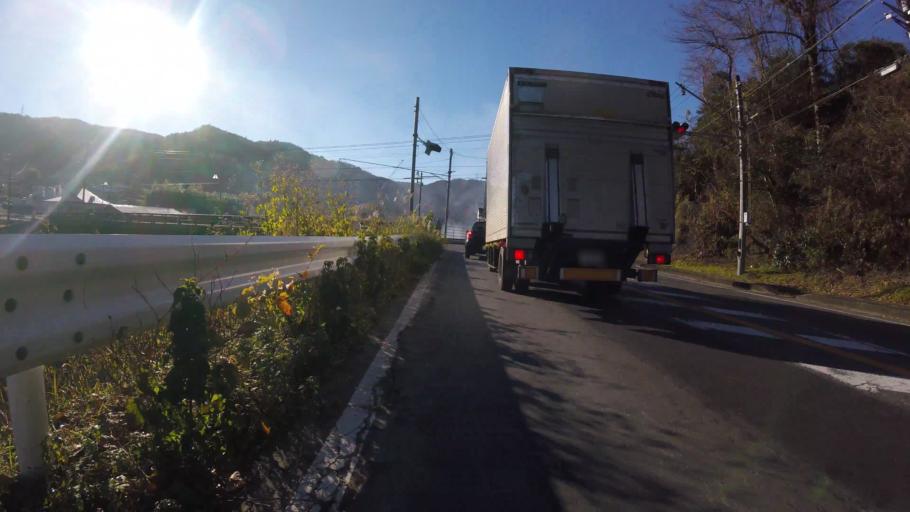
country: JP
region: Shizuoka
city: Heda
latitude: 34.9255
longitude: 138.9324
